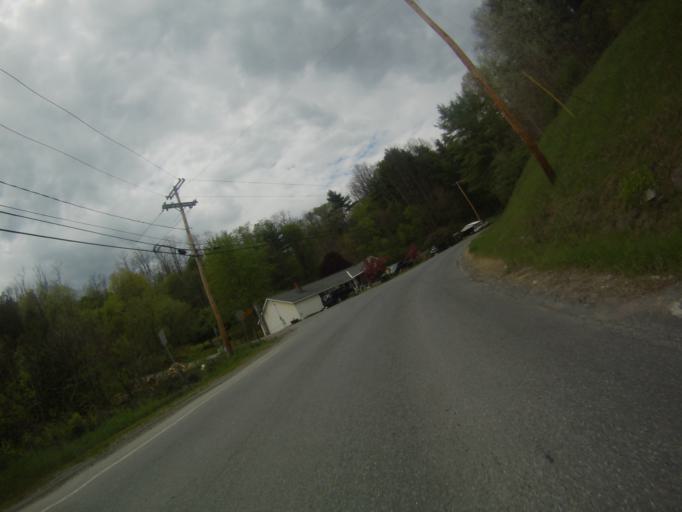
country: US
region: New York
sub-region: Essex County
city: Port Henry
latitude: 43.9442
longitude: -73.4717
